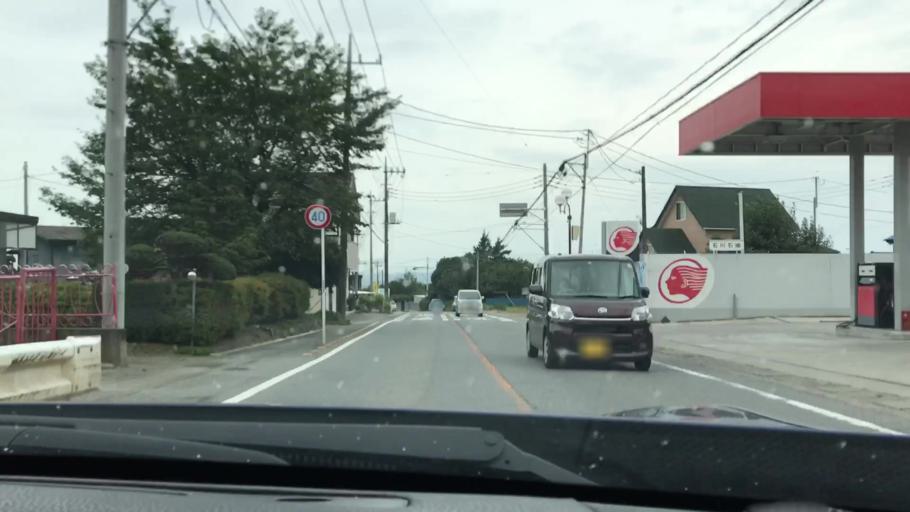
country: JP
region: Gunma
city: Kanekomachi
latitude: 36.3936
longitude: 138.9603
